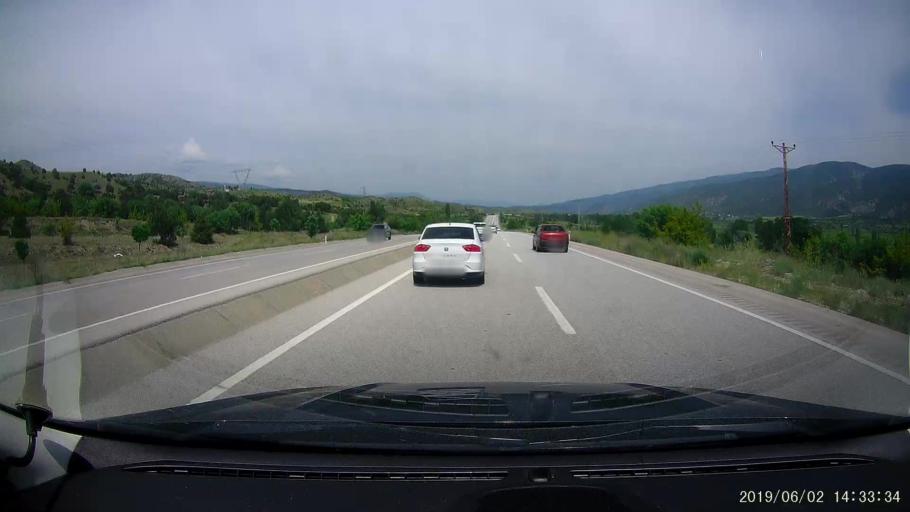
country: TR
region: Kastamonu
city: Tosya
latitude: 41.0323
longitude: 34.1734
